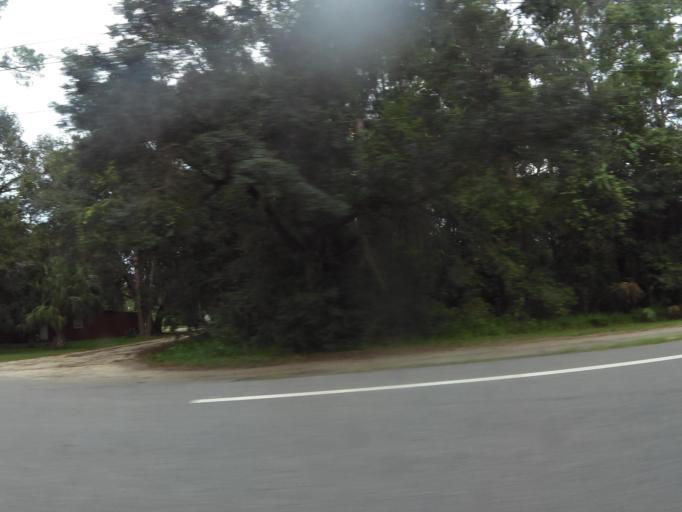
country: US
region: Florida
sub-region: Flagler County
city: Bunnell
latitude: 29.5054
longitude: -81.3099
